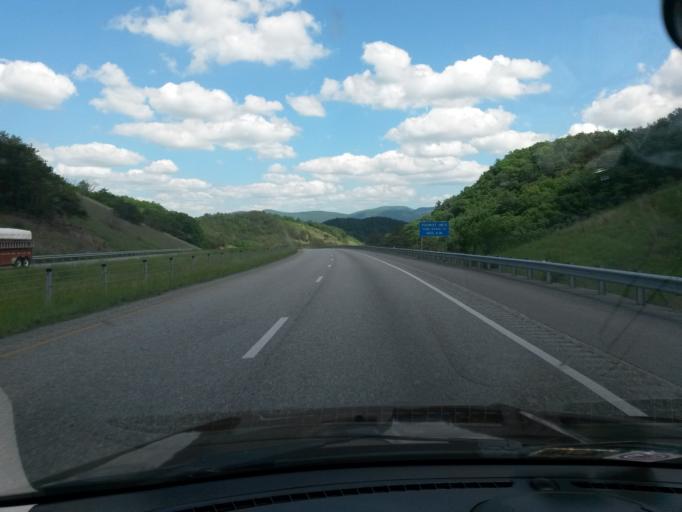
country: US
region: Virginia
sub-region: City of Covington
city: Covington
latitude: 37.7918
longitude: -80.0397
